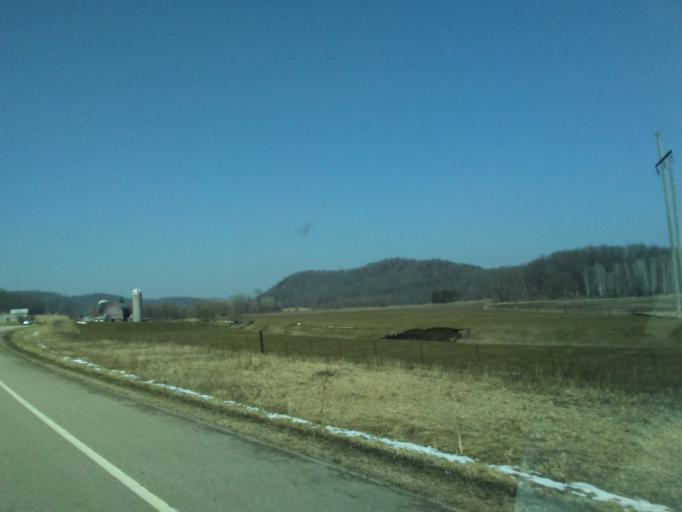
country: US
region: Wisconsin
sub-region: Richland County
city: Richland Center
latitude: 43.3433
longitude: -90.5371
